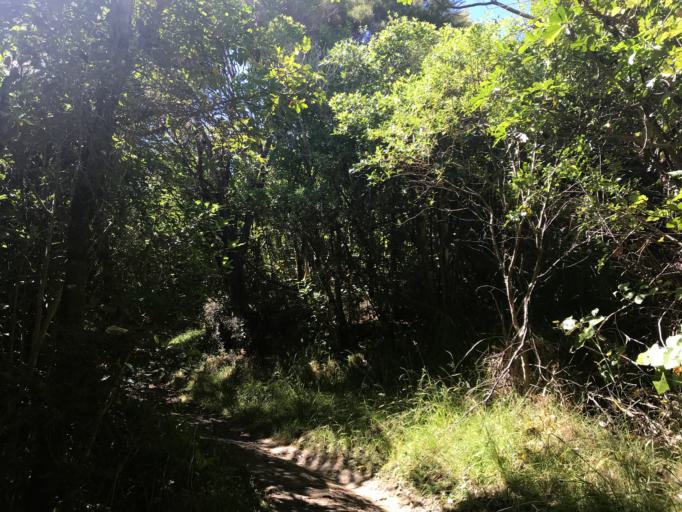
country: NZ
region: Marlborough
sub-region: Marlborough District
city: Picton
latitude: -41.2046
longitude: 174.0249
